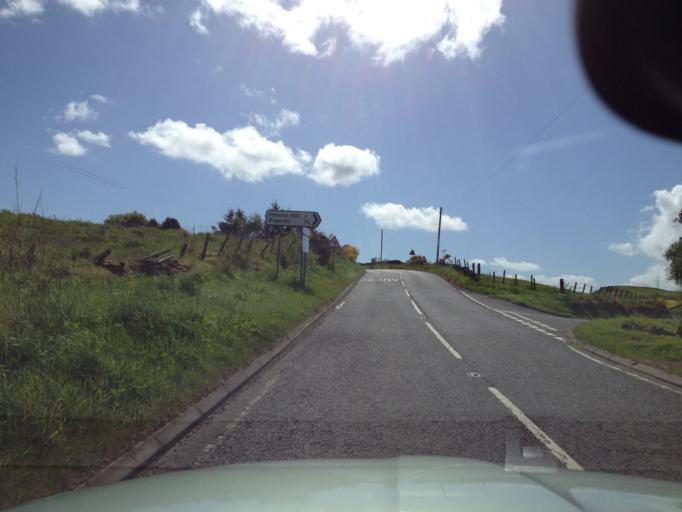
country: GB
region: Scotland
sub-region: Angus
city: Letham
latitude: 56.6868
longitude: -2.7899
